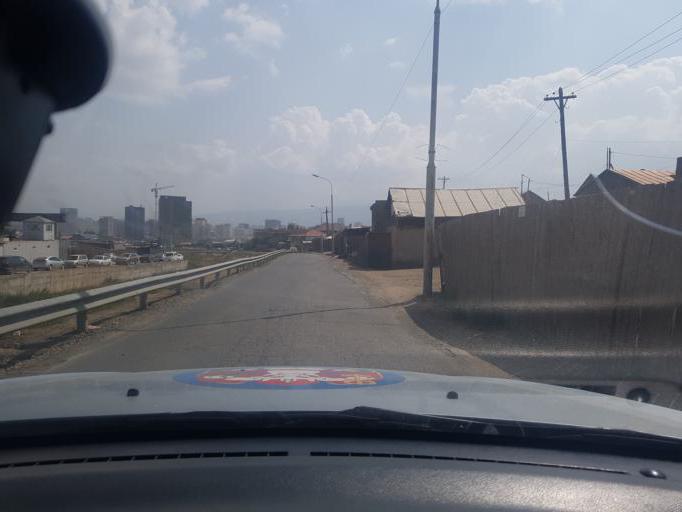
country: MN
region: Ulaanbaatar
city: Ulaanbaatar
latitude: 47.9375
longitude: 106.8998
